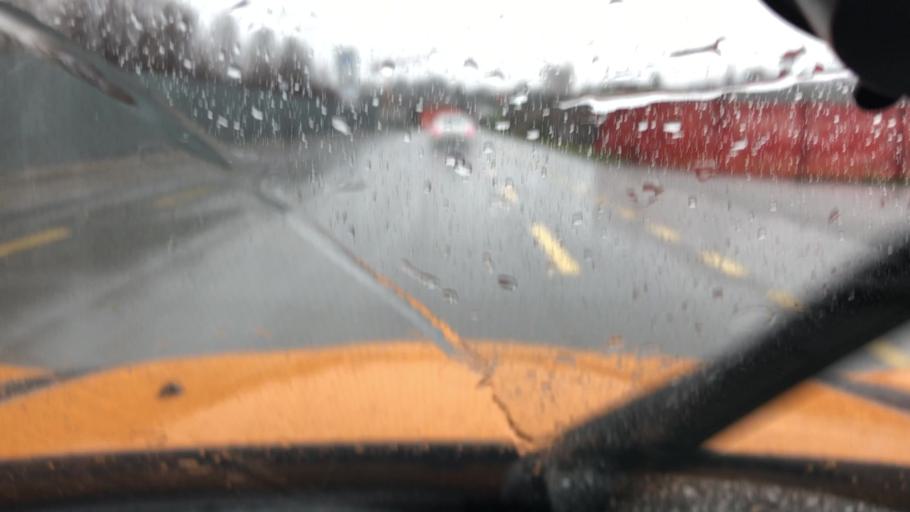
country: CH
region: Ticino
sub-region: Mendrisio District
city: Balerna
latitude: 45.8390
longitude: 9.0011
